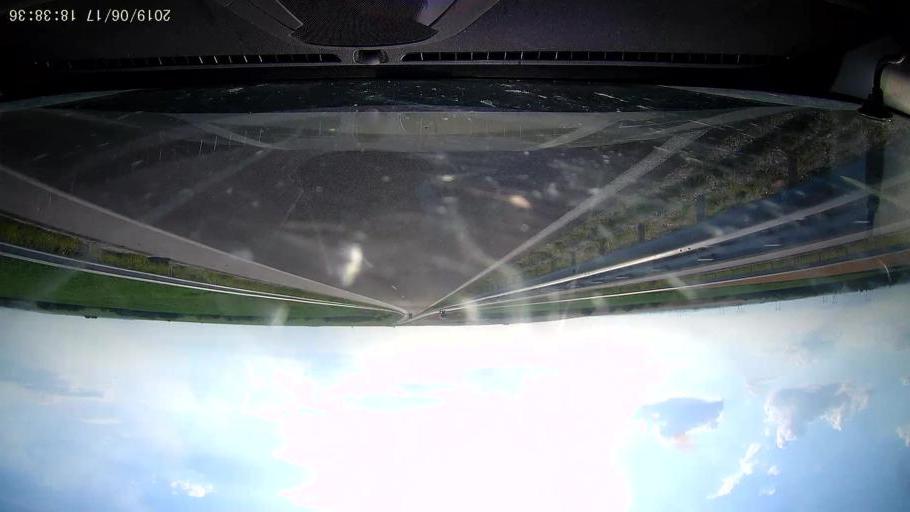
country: BG
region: Stara Zagora
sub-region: Obshtina Chirpan
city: Chirpan
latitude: 42.1379
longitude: 25.3323
